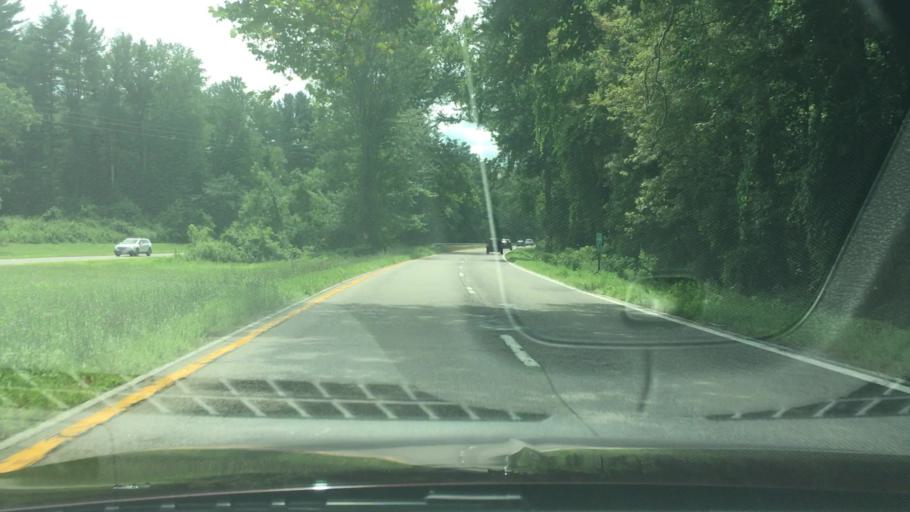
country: US
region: New York
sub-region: Dutchess County
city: Hillside Lake
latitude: 41.5862
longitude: -73.7678
